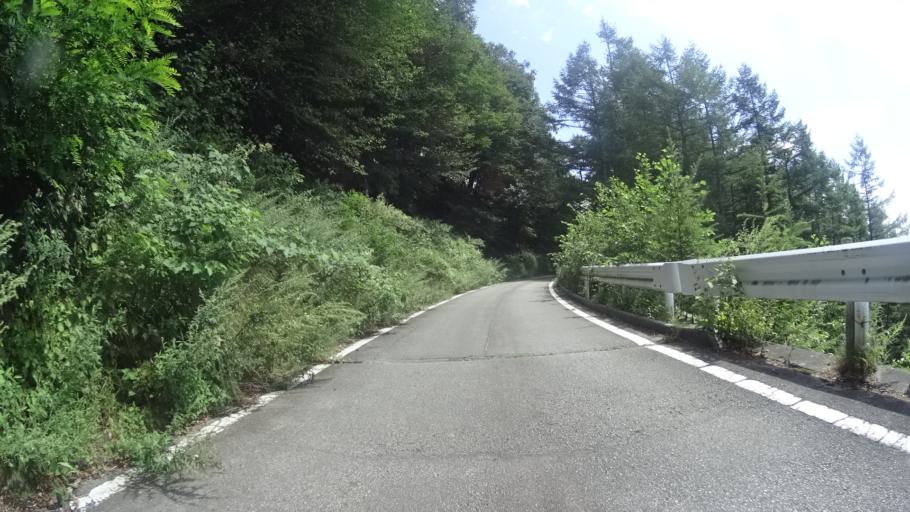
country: JP
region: Yamanashi
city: Enzan
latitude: 35.8311
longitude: 138.6390
